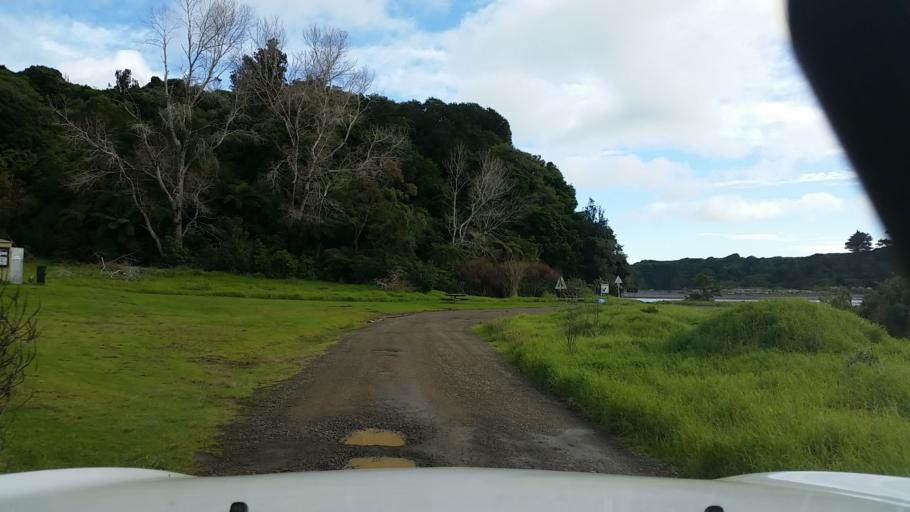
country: NZ
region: Taranaki
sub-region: New Plymouth District
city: Waitara
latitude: -38.8177
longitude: 174.5918
